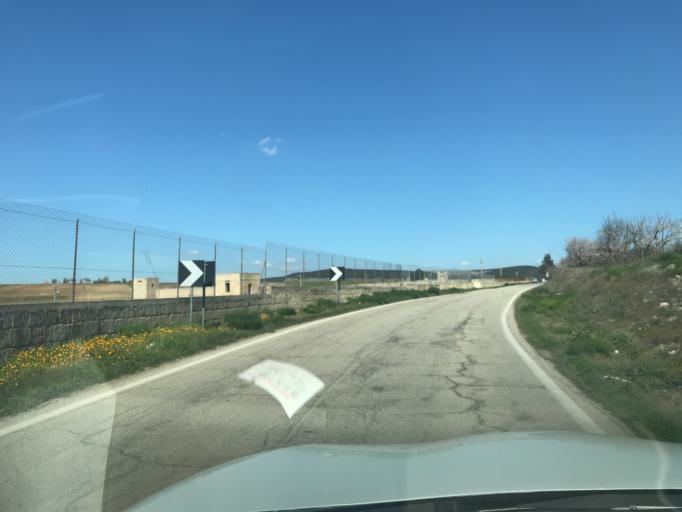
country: IT
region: Apulia
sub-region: Provincia di Bari
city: Gravina in Puglia
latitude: 40.8453
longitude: 16.4254
